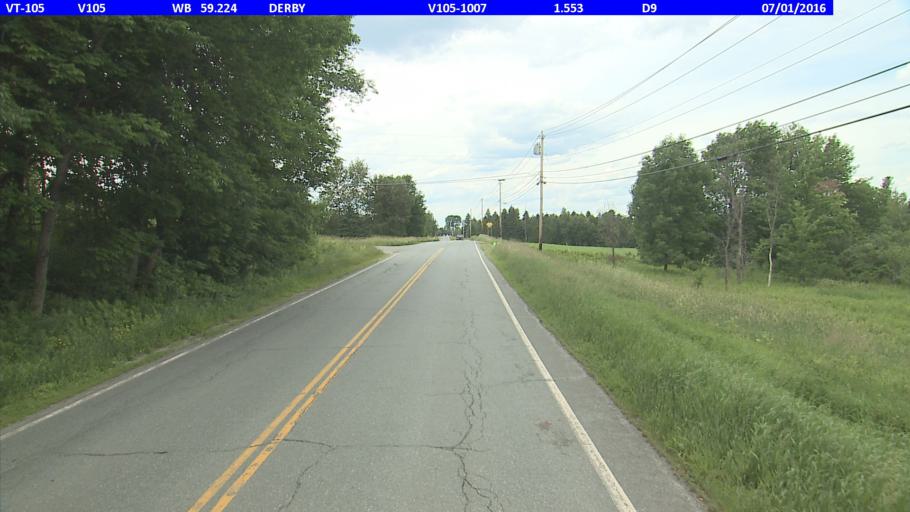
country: US
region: Vermont
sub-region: Orleans County
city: Newport
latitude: 44.9361
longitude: -72.1226
